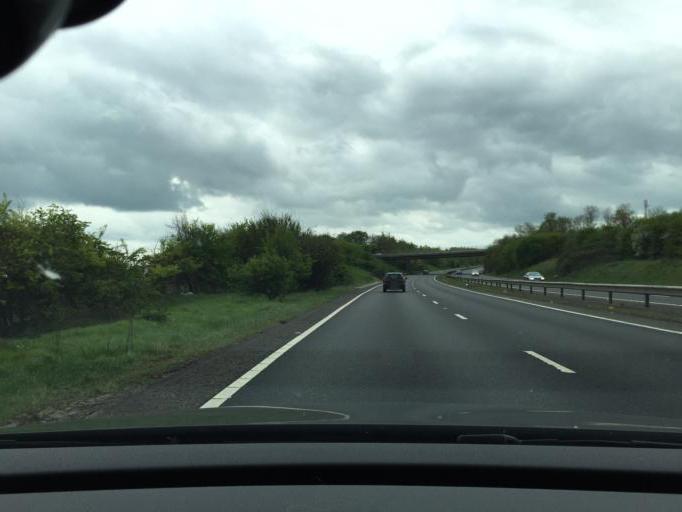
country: GB
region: England
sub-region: Oxfordshire
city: Harwell
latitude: 51.5933
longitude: -1.2789
